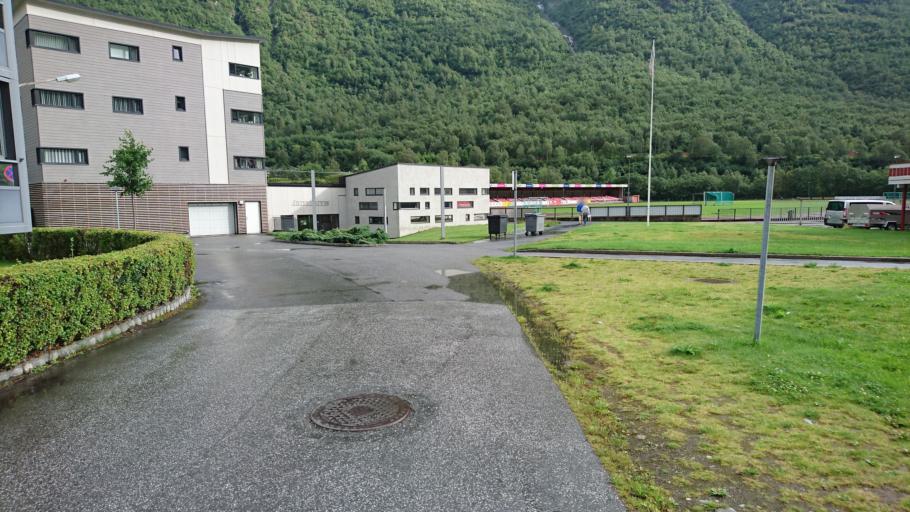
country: NO
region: Sogn og Fjordane
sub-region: Ardal
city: Farnes
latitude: 61.3091
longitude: 7.8074
